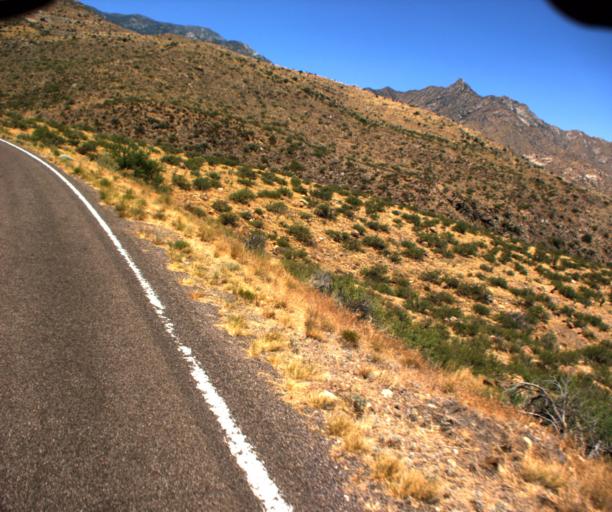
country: US
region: Arizona
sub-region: Graham County
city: Swift Trail Junction
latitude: 32.6903
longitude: -109.7618
